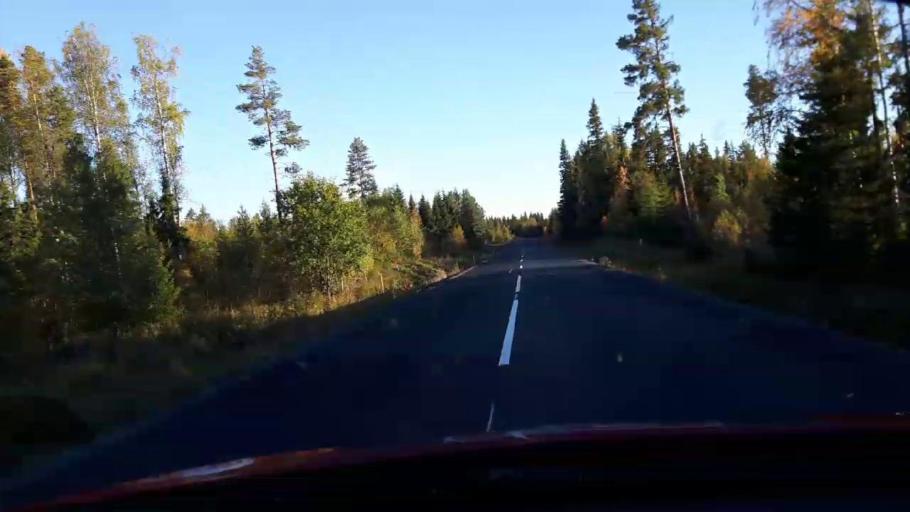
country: SE
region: Jaemtland
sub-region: OEstersunds Kommun
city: Lit
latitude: 63.4913
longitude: 14.8774
